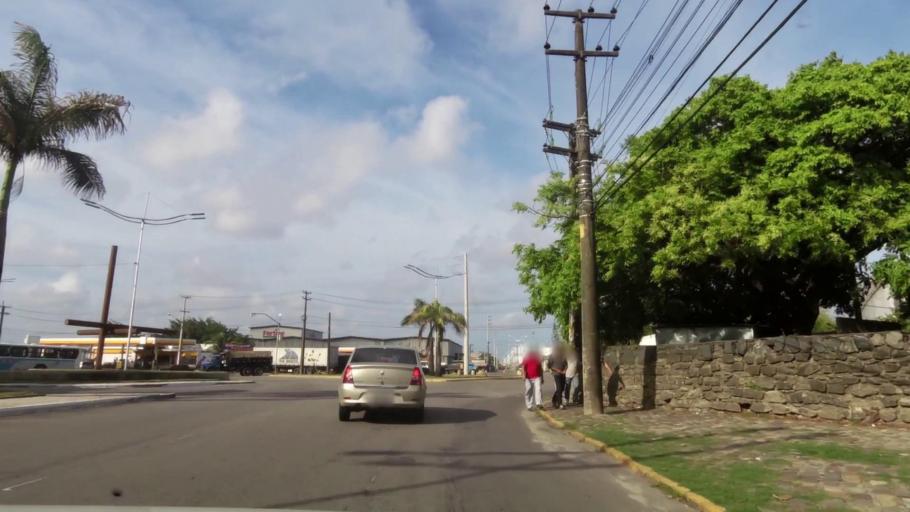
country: BR
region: Pernambuco
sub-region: Recife
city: Recife
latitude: -8.0501
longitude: -34.8705
